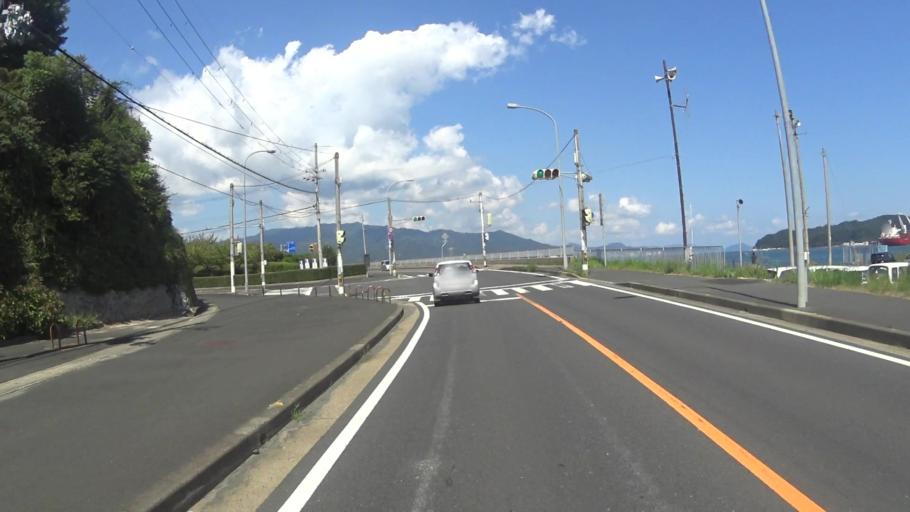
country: JP
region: Kyoto
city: Miyazu
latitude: 35.5443
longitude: 135.1902
